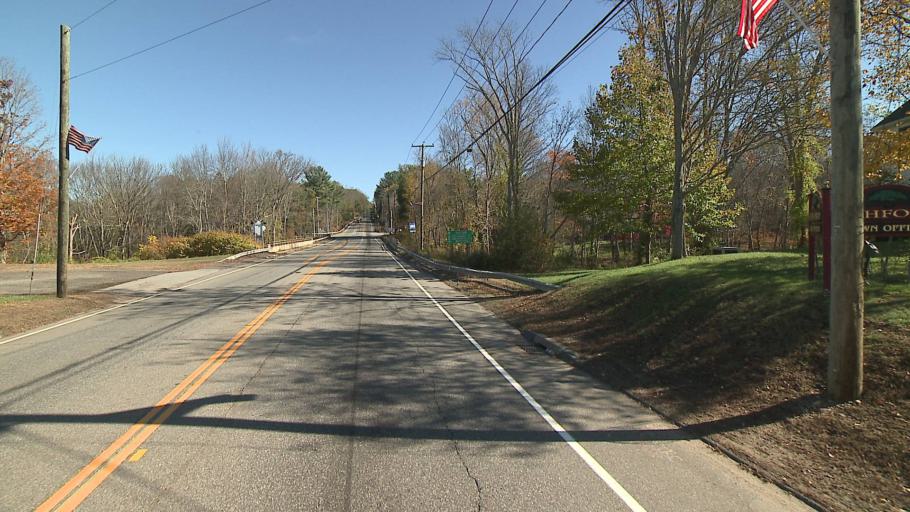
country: US
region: Connecticut
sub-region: Tolland County
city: Storrs
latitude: 41.8636
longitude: -72.1620
